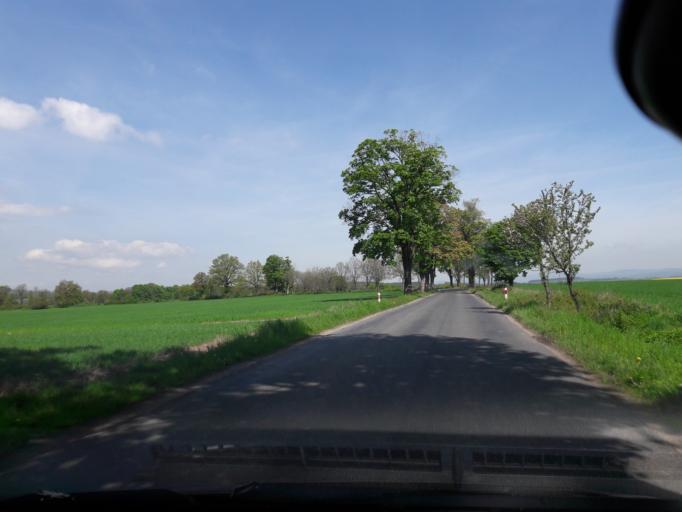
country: PL
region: Lower Silesian Voivodeship
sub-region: Powiat klodzki
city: Bystrzyca Klodzka
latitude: 50.3382
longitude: 16.5955
